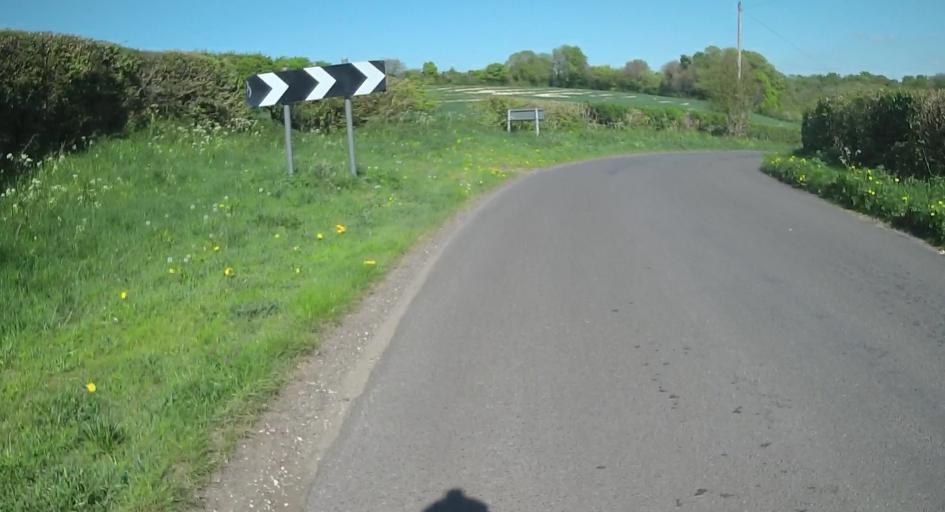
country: GB
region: England
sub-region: Hampshire
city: Four Marks
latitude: 51.1578
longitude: -1.0388
